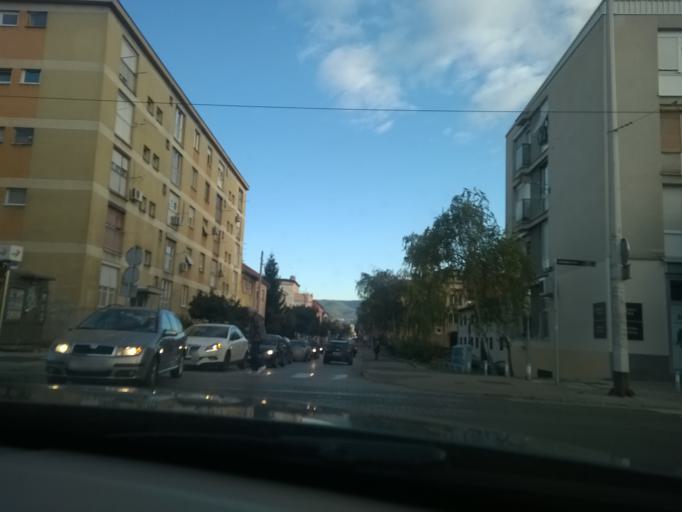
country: HR
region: Grad Zagreb
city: Jankomir
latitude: 45.7986
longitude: 15.9395
